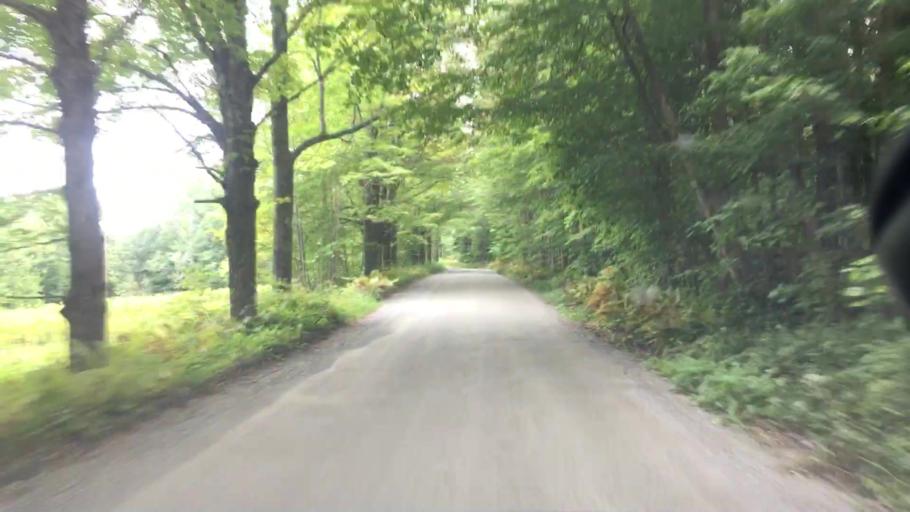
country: US
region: Vermont
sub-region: Windham County
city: Dover
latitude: 42.8527
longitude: -72.7773
